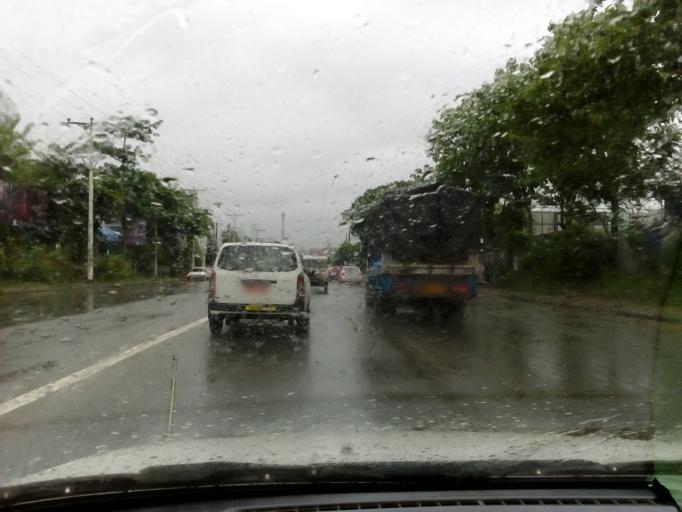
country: MM
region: Yangon
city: Yangon
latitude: 16.8188
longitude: 96.1725
